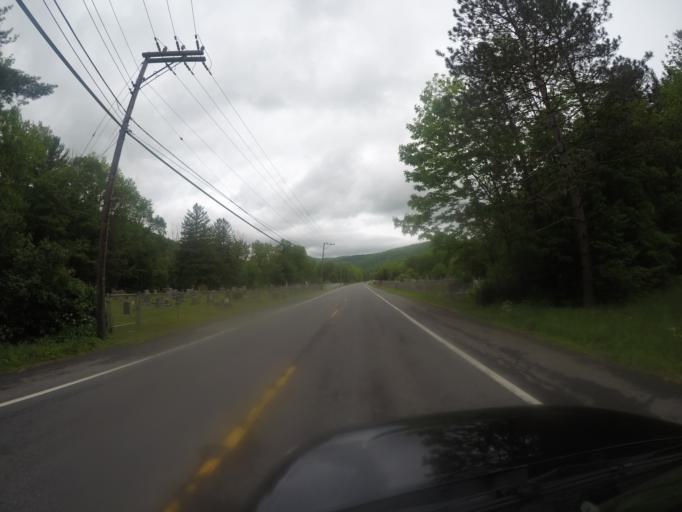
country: US
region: New York
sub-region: Ulster County
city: Shokan
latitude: 42.1045
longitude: -74.3494
